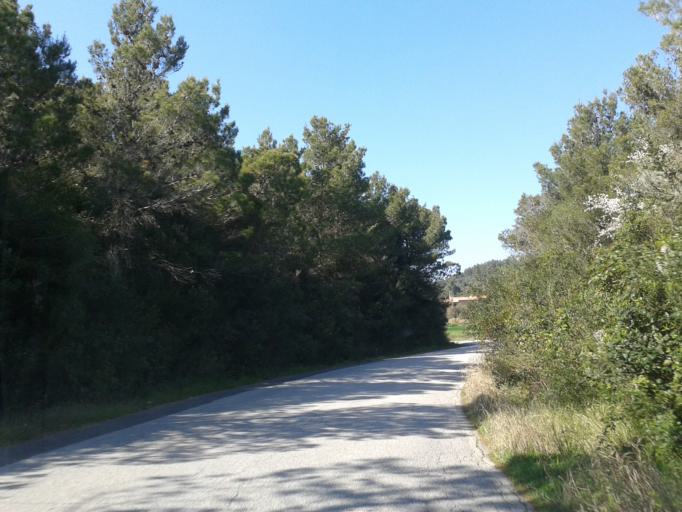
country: IT
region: Tuscany
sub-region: Provincia di Livorno
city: Quercianella
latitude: 43.4526
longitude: 10.4030
